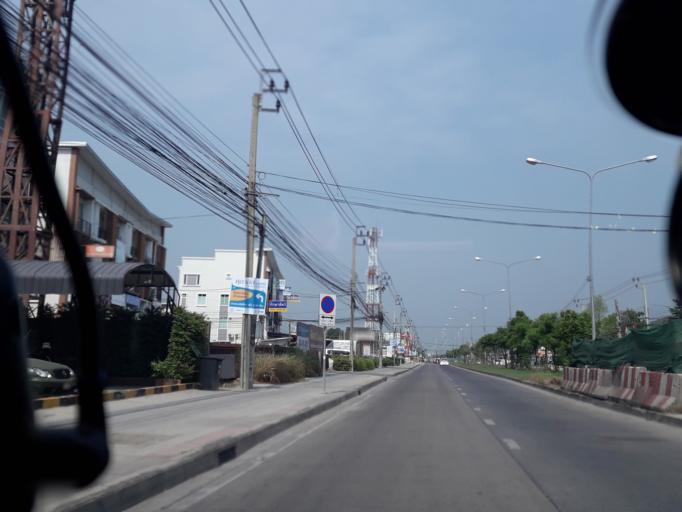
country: TH
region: Bangkok
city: Khlong Sam Wa
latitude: 13.8381
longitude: 100.7201
